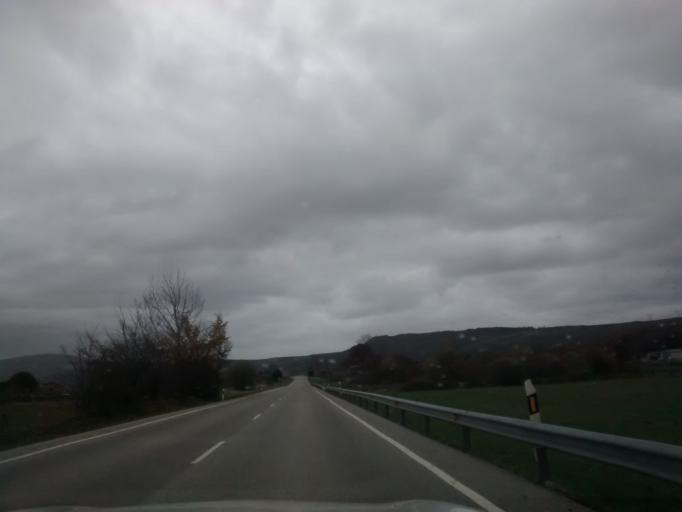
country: ES
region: Castille and Leon
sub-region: Provincia de Burgos
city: Arija
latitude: 43.0129
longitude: -3.8481
